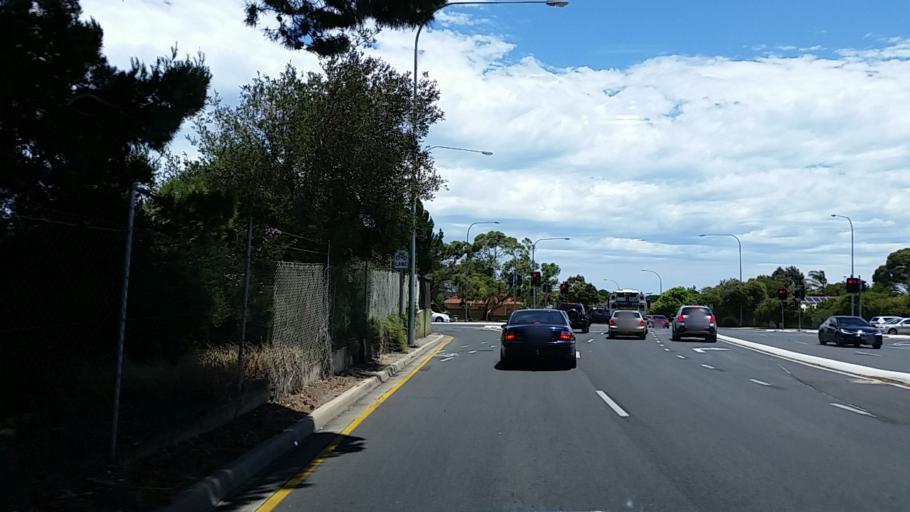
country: AU
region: South Australia
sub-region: Charles Sturt
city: Grange
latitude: -34.8921
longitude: 138.5054
